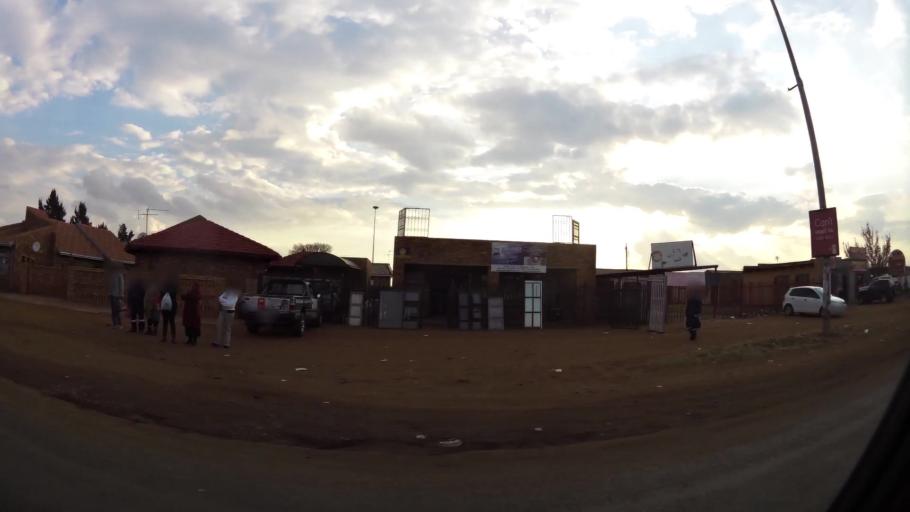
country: ZA
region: Gauteng
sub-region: City of Johannesburg Metropolitan Municipality
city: Orange Farm
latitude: -26.5920
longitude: 27.8472
